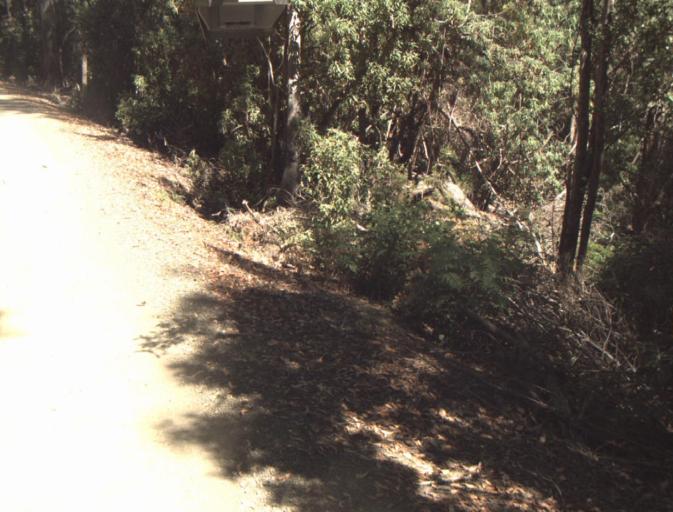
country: AU
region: Tasmania
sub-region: Dorset
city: Scottsdale
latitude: -41.3602
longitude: 147.3954
